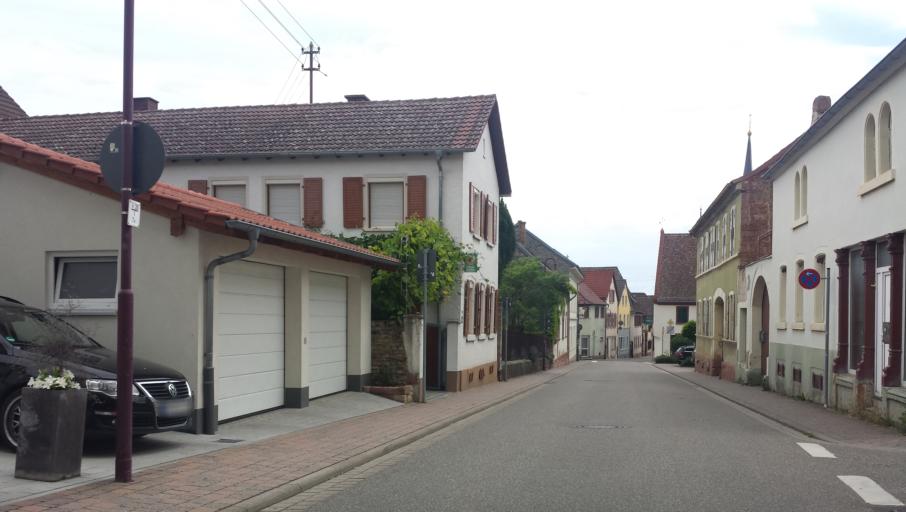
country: DE
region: Rheinland-Pfalz
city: Maikammer
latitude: 49.3066
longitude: 8.1289
